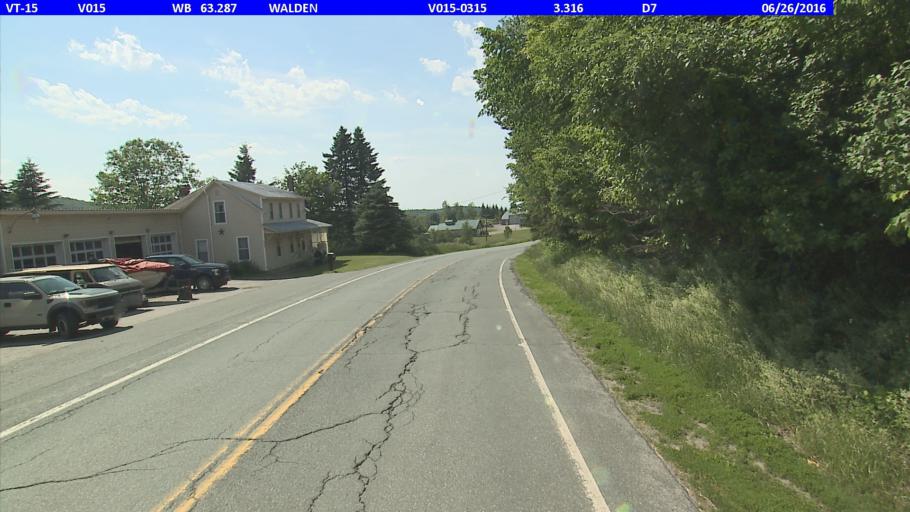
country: US
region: Vermont
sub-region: Caledonia County
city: Hardwick
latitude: 44.4537
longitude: -72.2586
